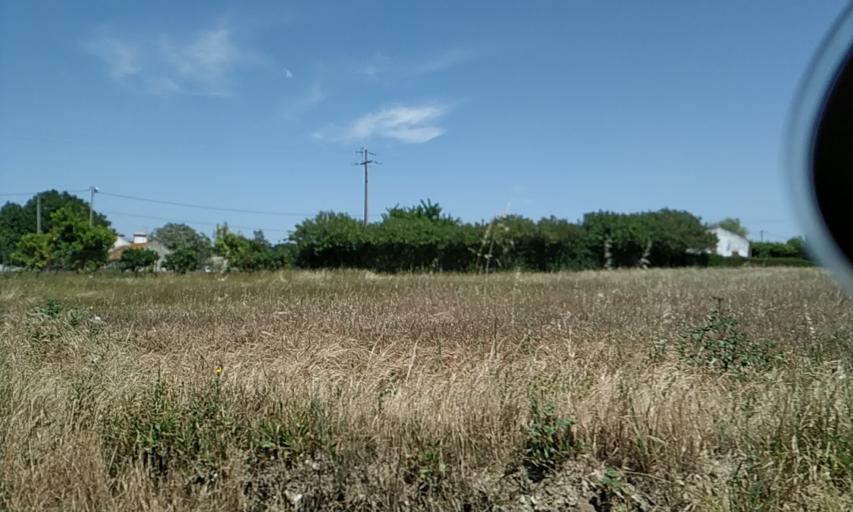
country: PT
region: Setubal
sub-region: Palmela
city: Pinhal Novo
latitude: 38.6472
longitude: -8.7443
